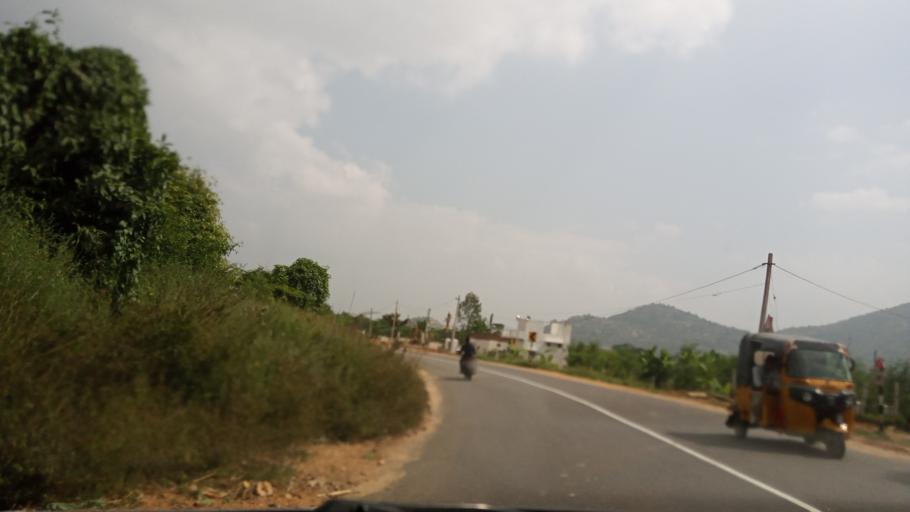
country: IN
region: Andhra Pradesh
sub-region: Chittoor
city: Madanapalle
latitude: 13.6343
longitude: 78.6159
